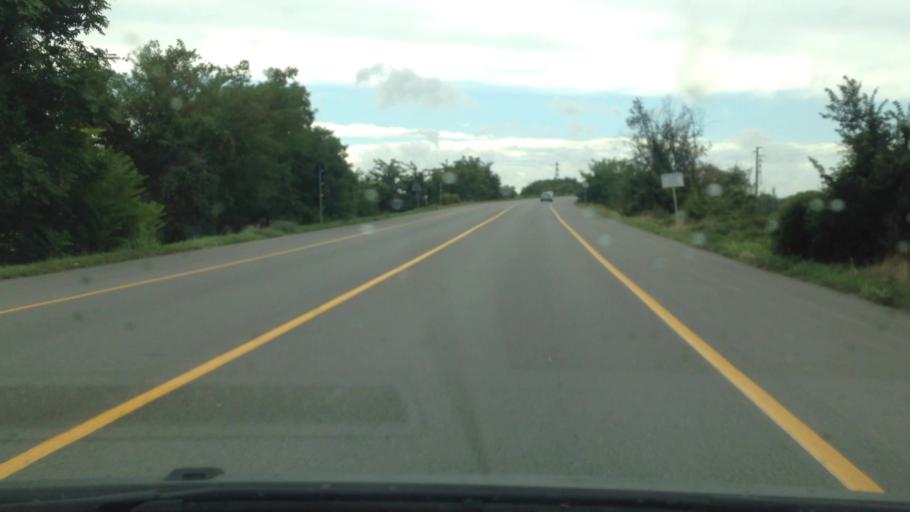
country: IT
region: Piedmont
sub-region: Provincia di Alessandria
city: Tortona
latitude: 44.9003
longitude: 8.8392
